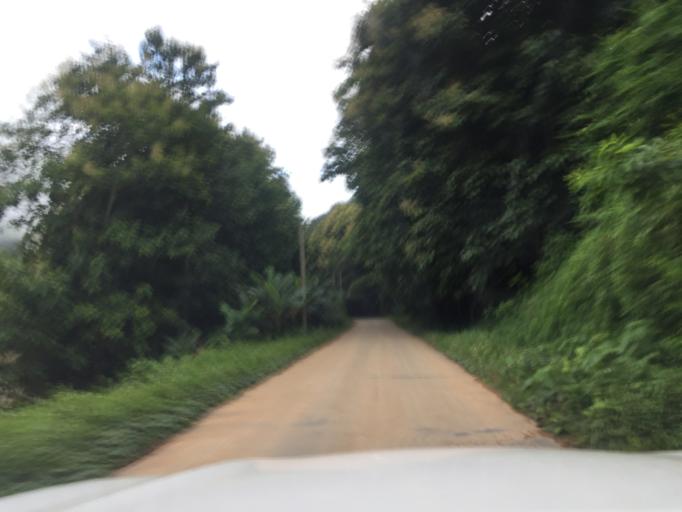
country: LA
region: Phongsali
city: Khoa
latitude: 21.0803
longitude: 102.3735
